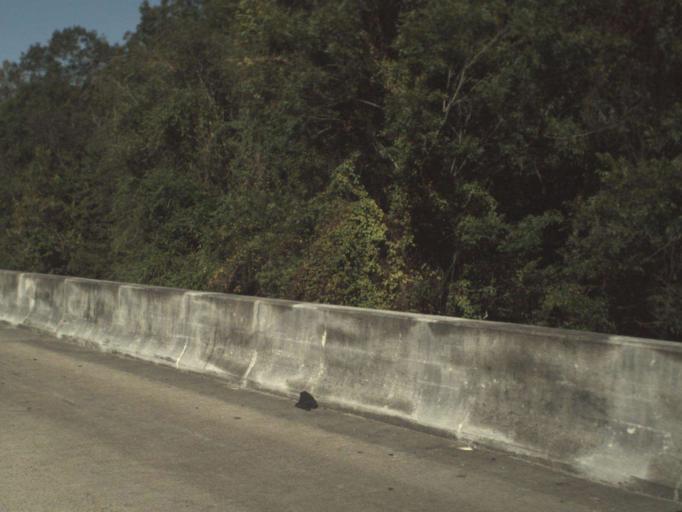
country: US
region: Florida
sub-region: Holmes County
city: Bonifay
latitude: 30.7573
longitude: -85.8200
